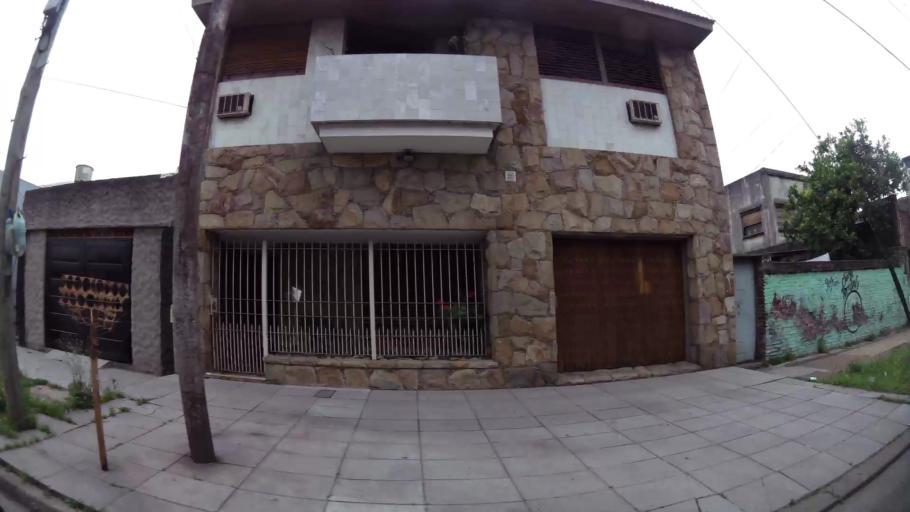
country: AR
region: Buenos Aires
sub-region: Partido de Avellaneda
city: Avellaneda
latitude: -34.6875
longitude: -58.3655
